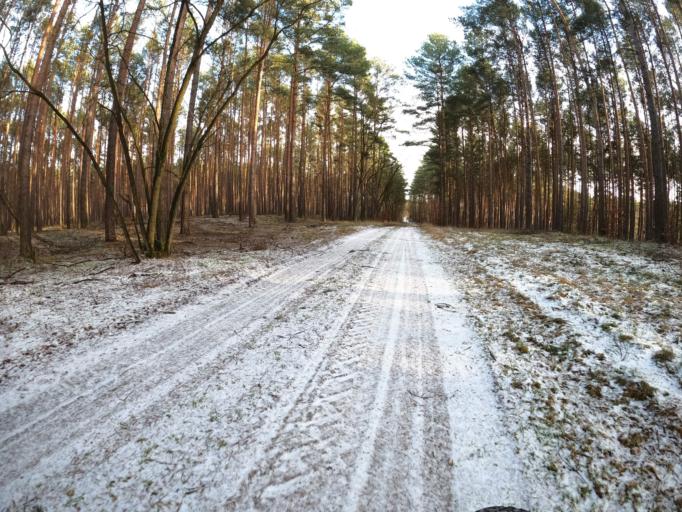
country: PL
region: Lubusz
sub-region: Powiat slubicki
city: Cybinka
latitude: 52.2298
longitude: 14.8351
